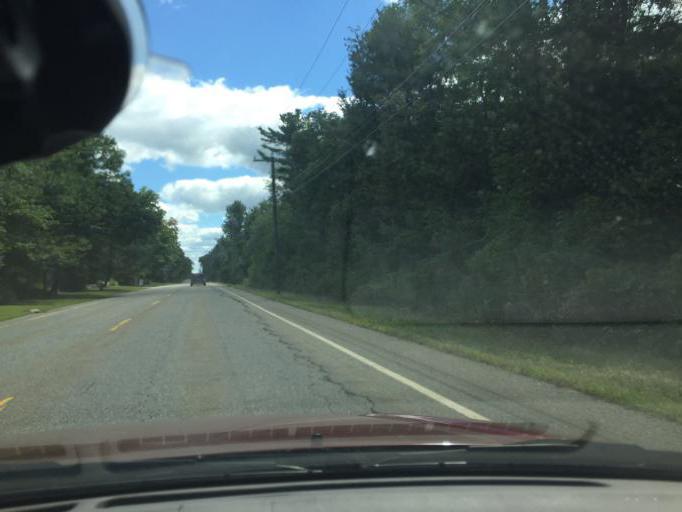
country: US
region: Connecticut
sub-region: Litchfield County
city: Litchfield
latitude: 41.8069
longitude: -73.2159
